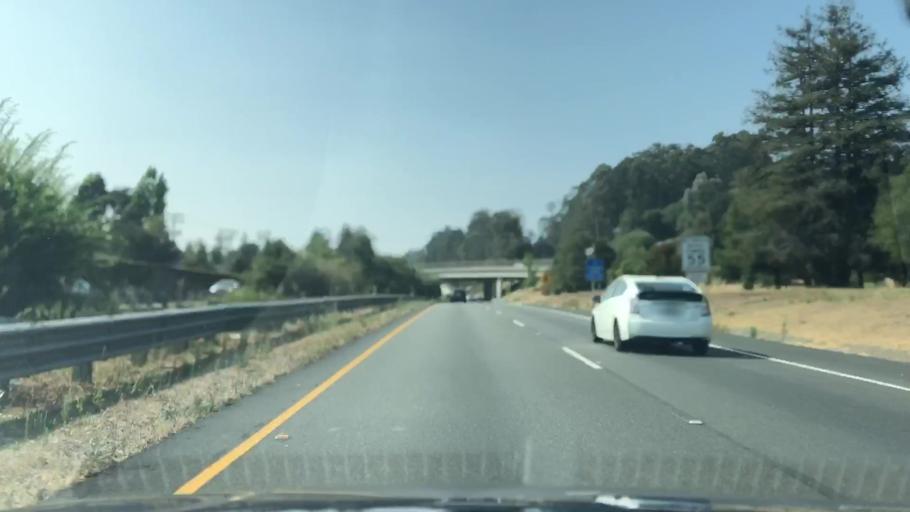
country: US
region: California
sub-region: Alameda County
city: Piedmont
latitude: 37.7964
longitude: -122.1835
